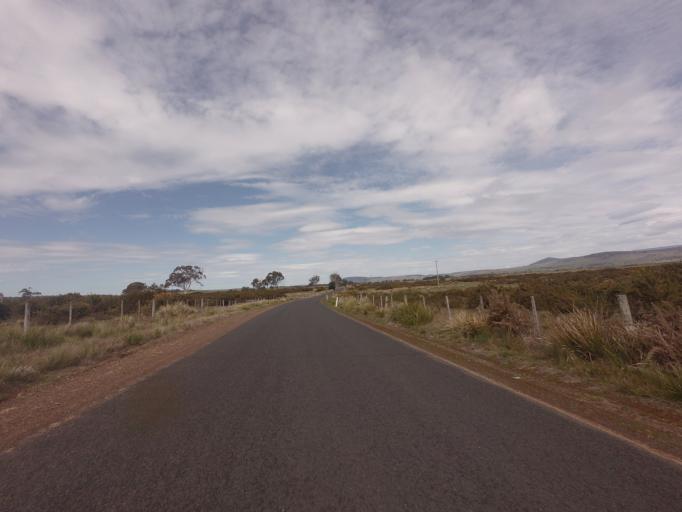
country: AU
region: Tasmania
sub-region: Northern Midlands
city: Evandale
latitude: -41.8340
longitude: 147.3288
